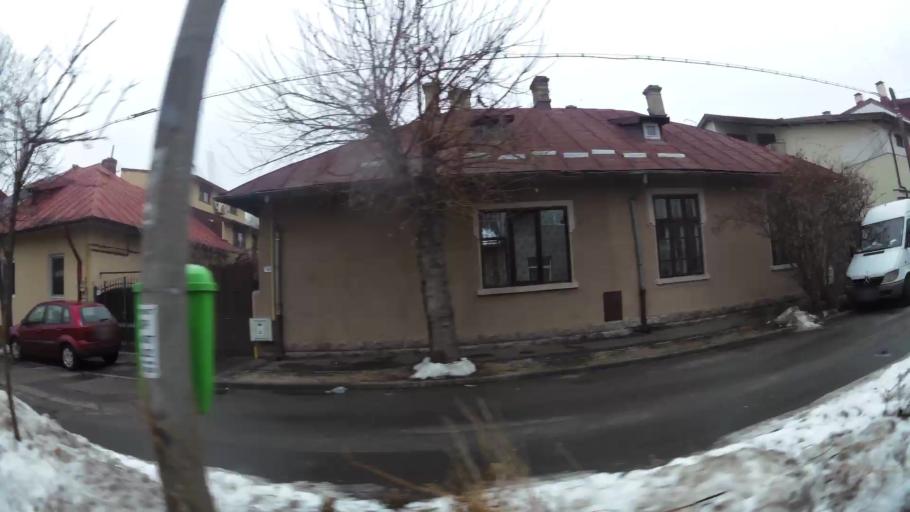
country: RO
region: Ilfov
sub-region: Comuna Chiajna
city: Rosu
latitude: 44.4466
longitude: 26.0557
